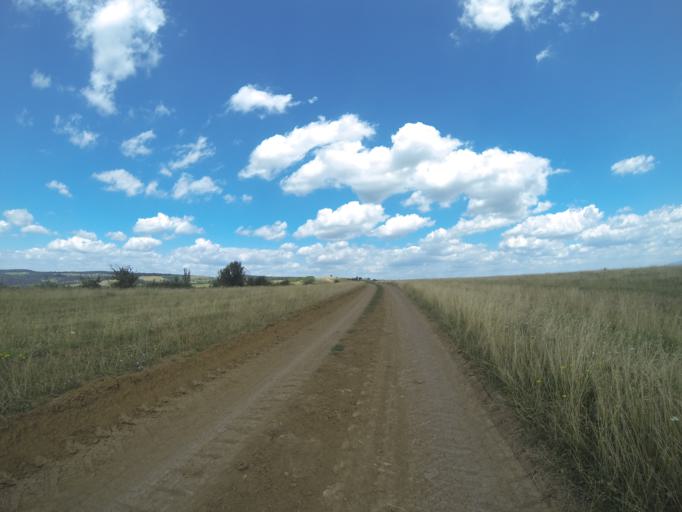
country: RO
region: Brasov
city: Fogarasch
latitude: 45.8587
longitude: 24.9961
